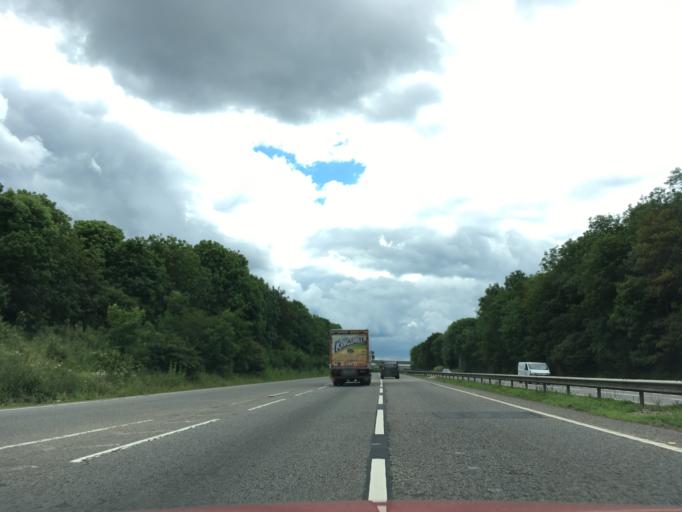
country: GB
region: England
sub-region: Milton Keynes
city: Loughton
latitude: 52.0352
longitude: -0.7783
